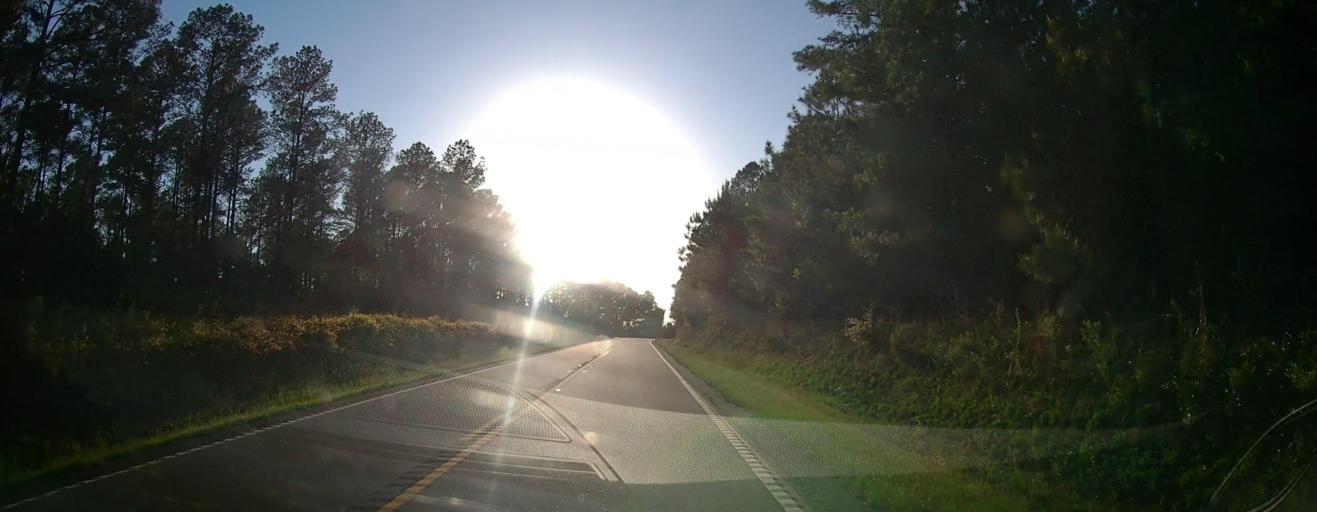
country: US
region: Georgia
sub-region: Schley County
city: Ellaville
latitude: 32.3224
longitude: -84.3159
